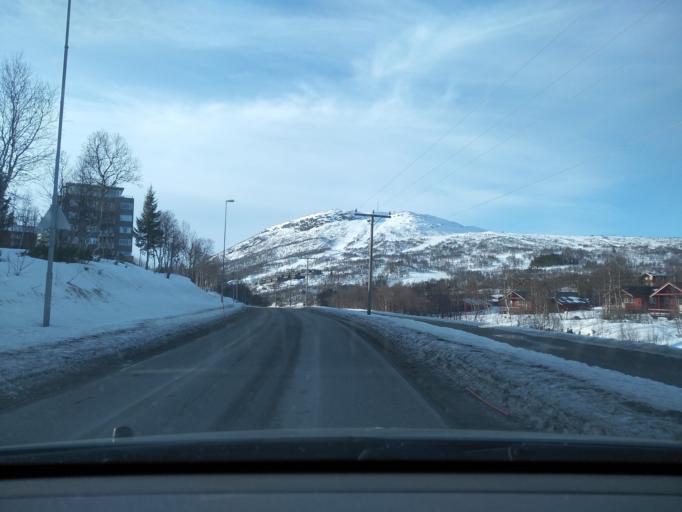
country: NO
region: Aust-Agder
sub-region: Bykle
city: Hovden
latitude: 59.5673
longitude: 7.3631
